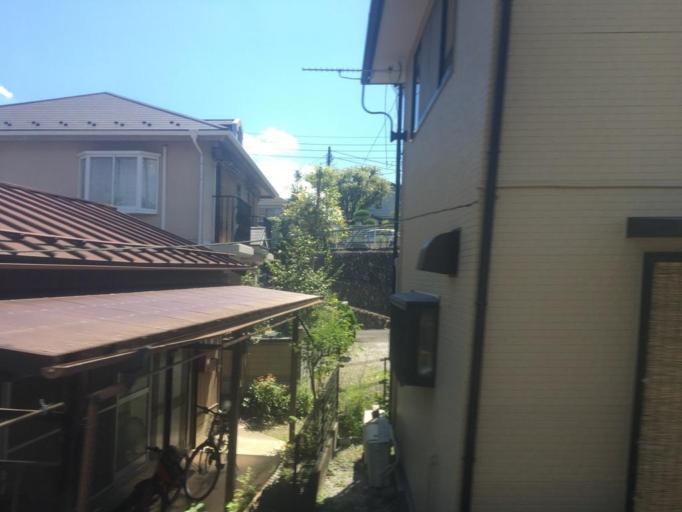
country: JP
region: Saitama
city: Chichibu
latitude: 35.9944
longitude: 139.0845
